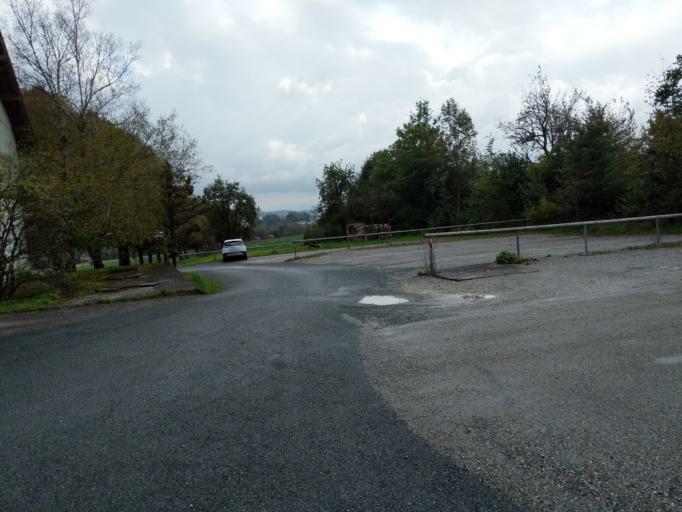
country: DE
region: Bavaria
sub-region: Upper Bavaria
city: Ebersberg
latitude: 48.0887
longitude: 11.9607
